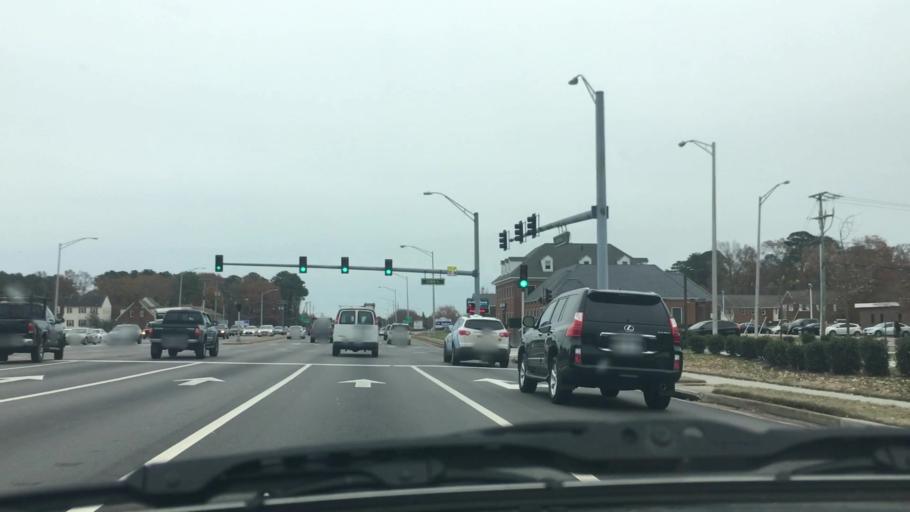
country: US
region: Virginia
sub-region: City of Chesapeake
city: Chesapeake
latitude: 36.8264
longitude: -76.1314
